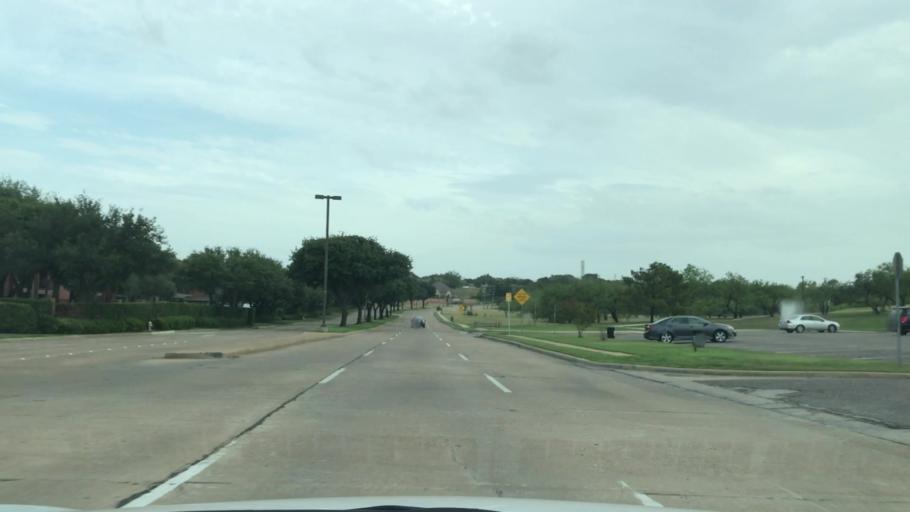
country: US
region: Texas
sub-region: Dallas County
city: Irving
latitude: 32.8616
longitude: -96.9767
